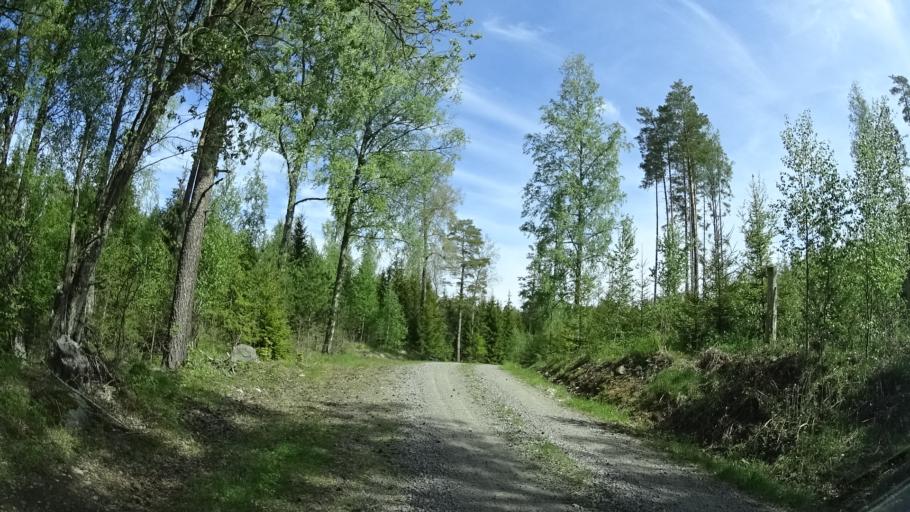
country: SE
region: OEstergoetland
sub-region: Finspangs Kommun
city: Finspang
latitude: 58.8031
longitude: 15.8386
